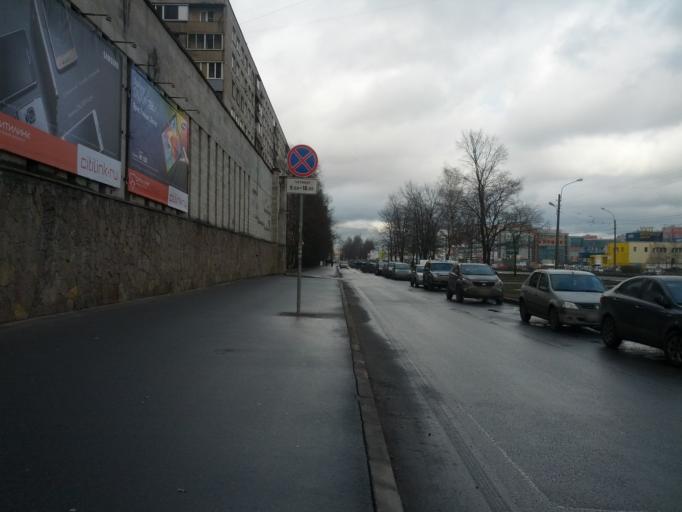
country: RU
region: Leningrad
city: Rybatskoye
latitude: 59.8975
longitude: 30.4906
